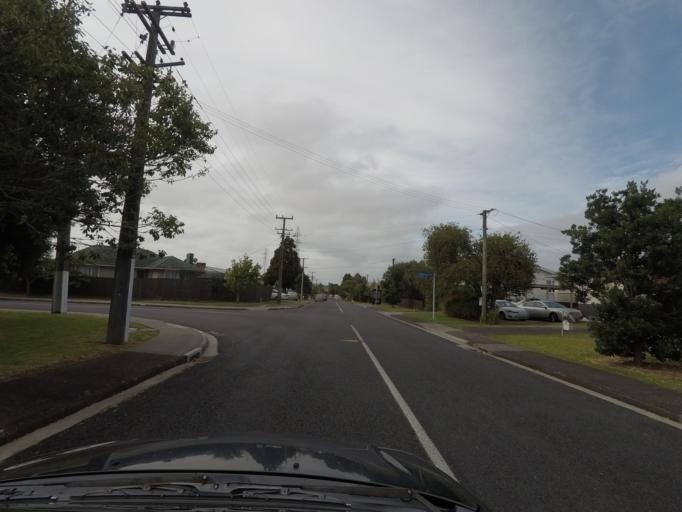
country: NZ
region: Auckland
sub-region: Auckland
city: Rosebank
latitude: -36.8936
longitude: 174.6657
